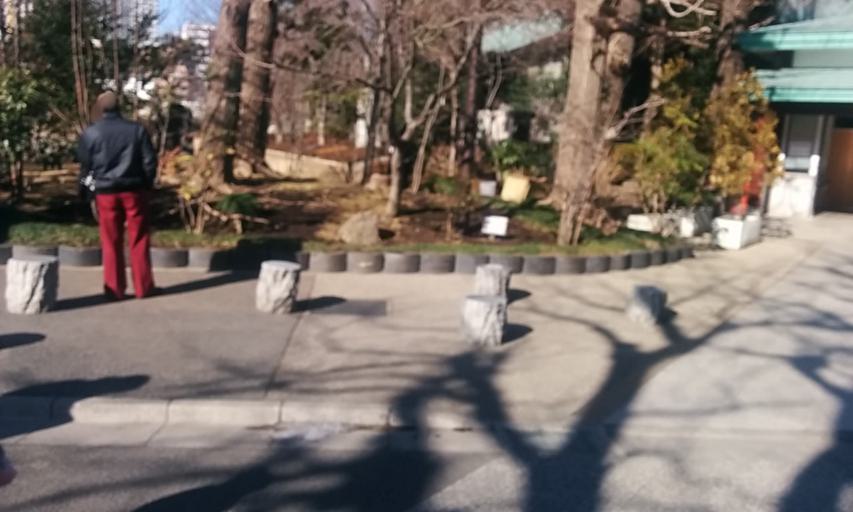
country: JP
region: Tokyo
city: Urayasu
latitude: 35.7154
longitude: 139.7971
